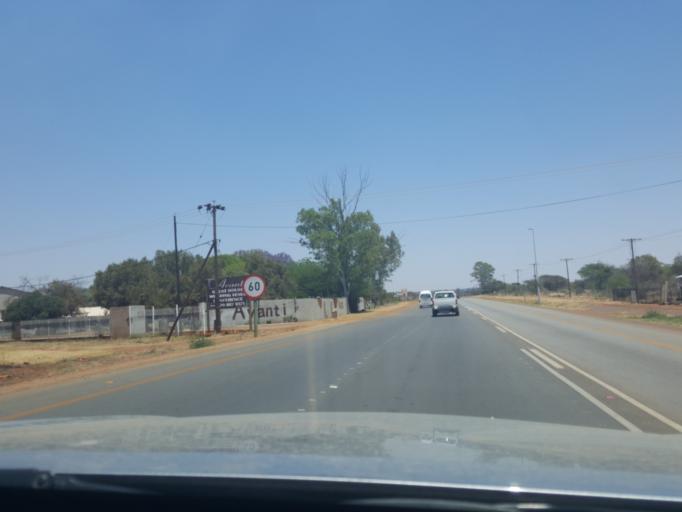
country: ZA
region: North-West
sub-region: Ngaka Modiri Molema District Municipality
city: Zeerust
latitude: -25.5537
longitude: 26.0704
